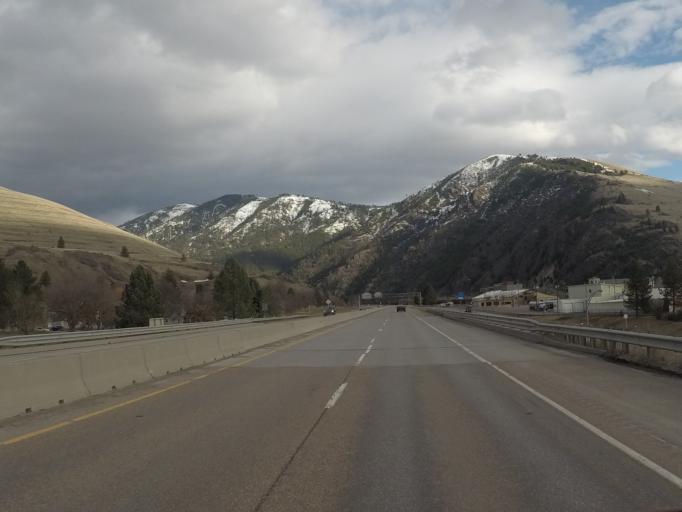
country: US
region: Montana
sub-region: Missoula County
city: Missoula
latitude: 46.8708
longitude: -113.9818
